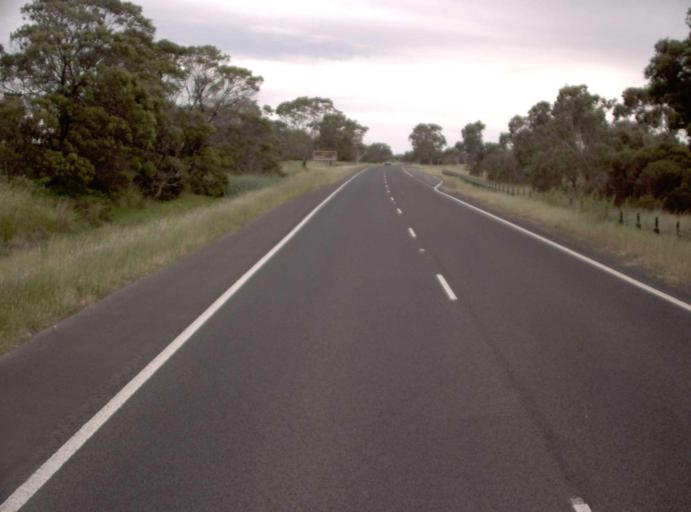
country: AU
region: Victoria
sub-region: Casey
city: Blind Bight
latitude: -38.1818
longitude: 145.3406
